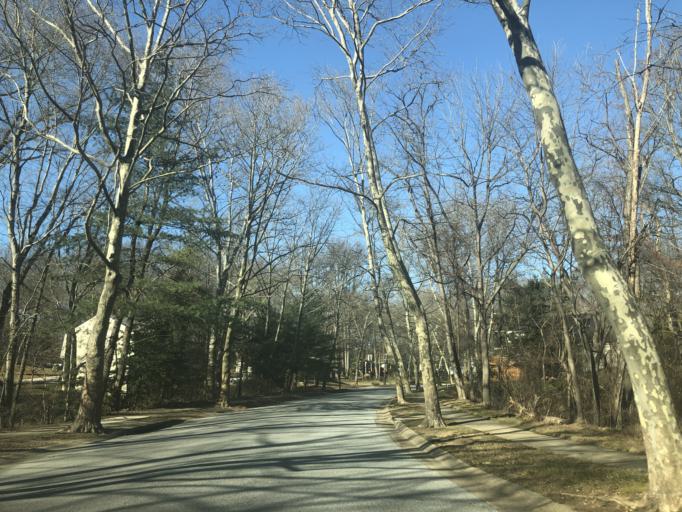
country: US
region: Maryland
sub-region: Howard County
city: Riverside
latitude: 39.1946
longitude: -76.8480
